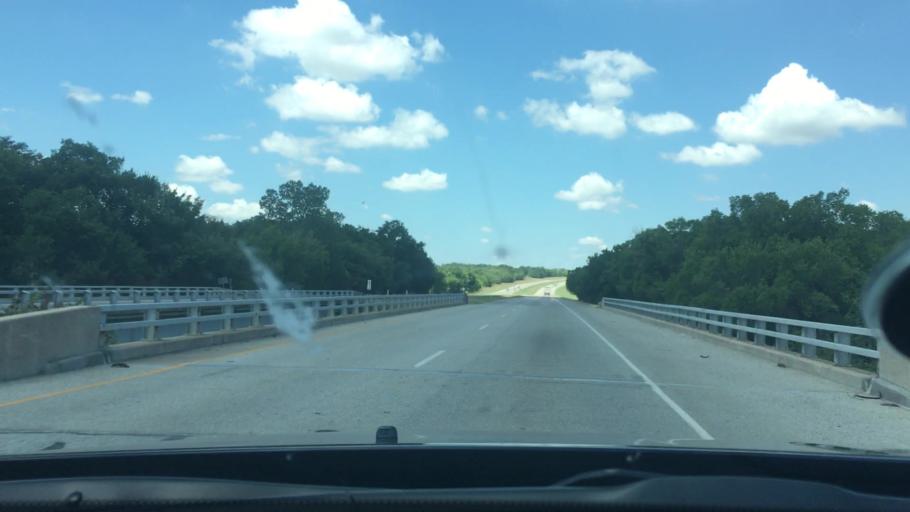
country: US
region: Oklahoma
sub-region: Carter County
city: Wilson
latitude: 34.1739
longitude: -97.3721
